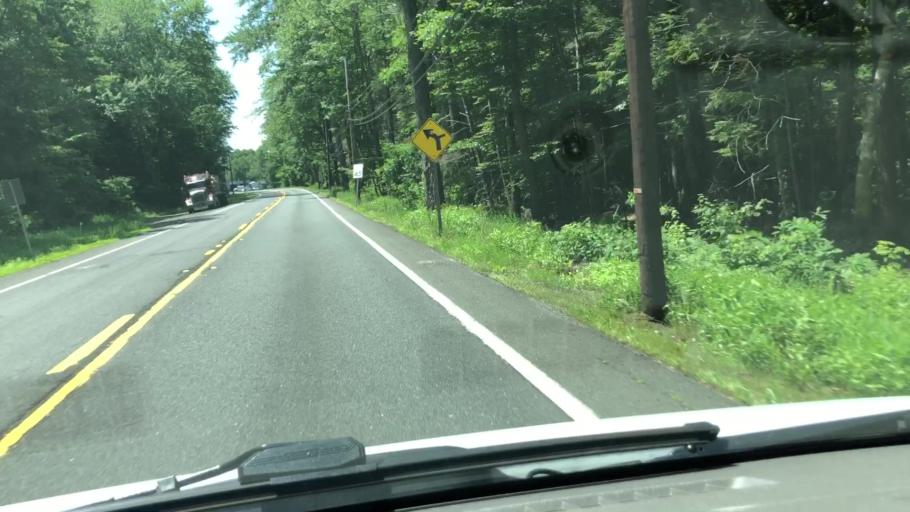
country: US
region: Massachusetts
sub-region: Franklin County
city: Whately
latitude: 42.4537
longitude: -72.6256
